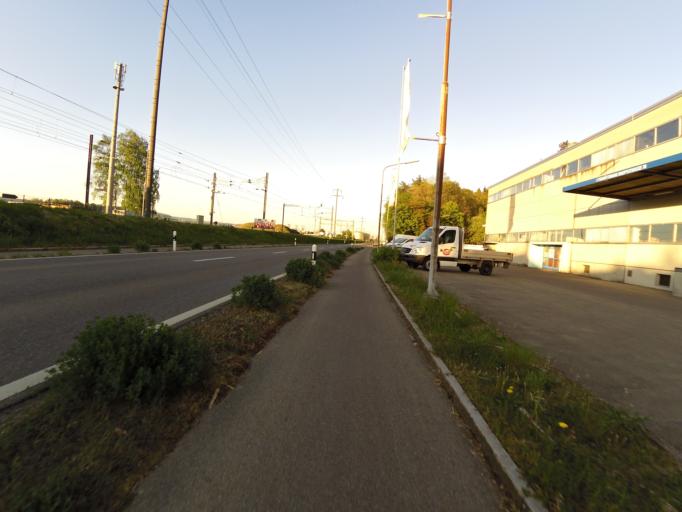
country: CH
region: Thurgau
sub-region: Frauenfeld District
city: Gachnang
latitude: 47.5484
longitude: 8.8489
